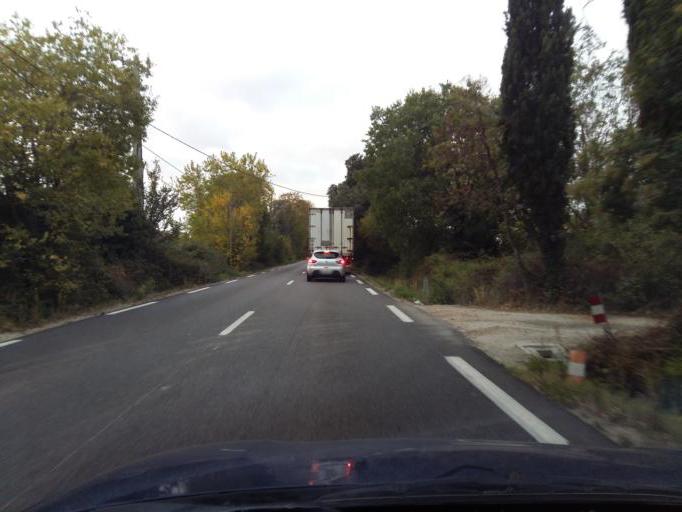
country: FR
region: Provence-Alpes-Cote d'Azur
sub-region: Departement des Bouches-du-Rhone
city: Miramas
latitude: 43.6163
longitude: 5.0133
